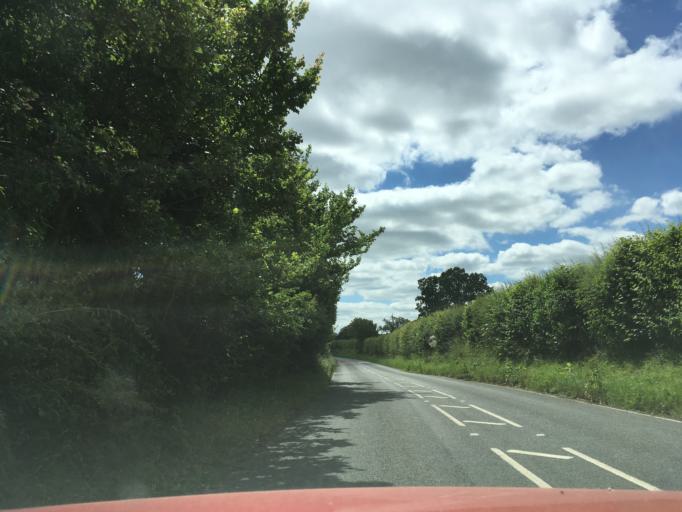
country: GB
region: England
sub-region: West Berkshire
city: Welford
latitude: 51.4382
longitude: -1.3904
